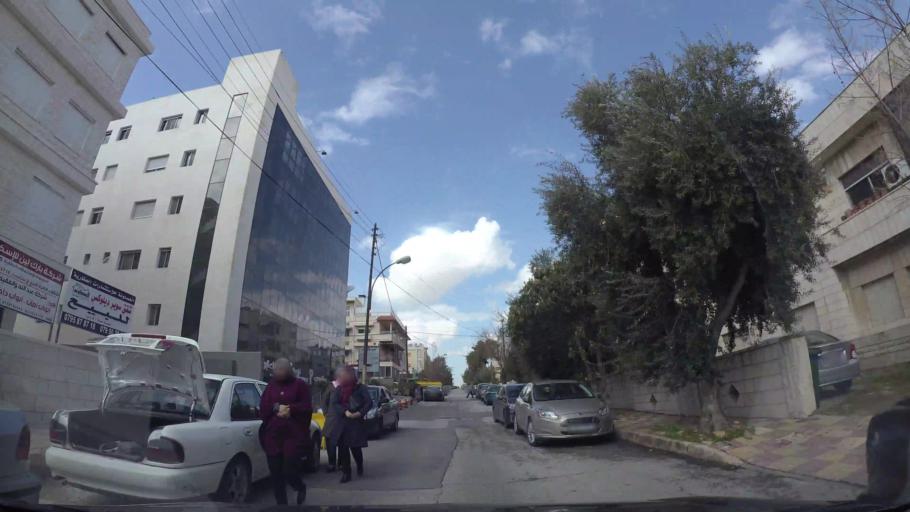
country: JO
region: Amman
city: Amman
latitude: 31.9697
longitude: 35.8945
